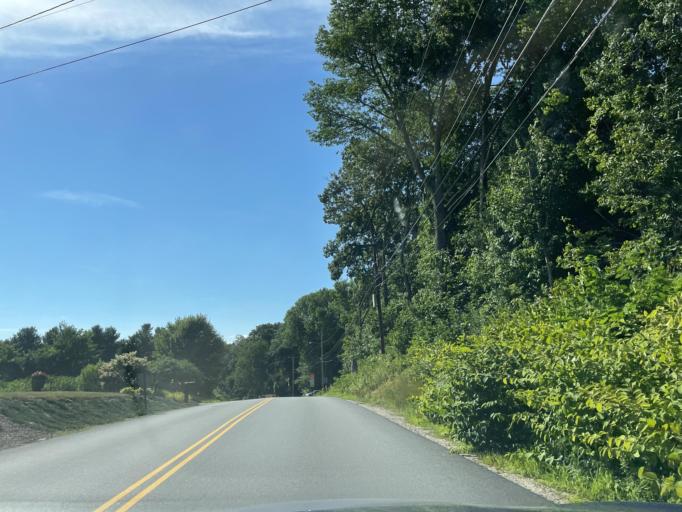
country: US
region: Massachusetts
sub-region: Worcester County
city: Charlton
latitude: 42.1341
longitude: -71.9406
